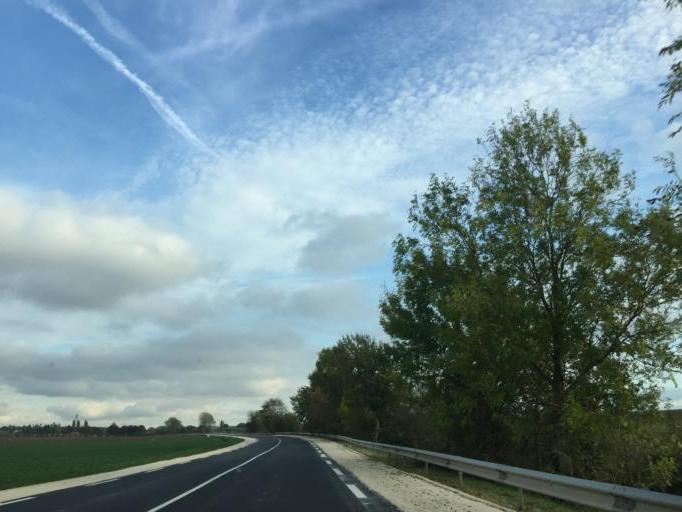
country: FR
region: Ile-de-France
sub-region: Departement de Seine-et-Marne
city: Jouy-le-Chatel
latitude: 48.6896
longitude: 3.0919
